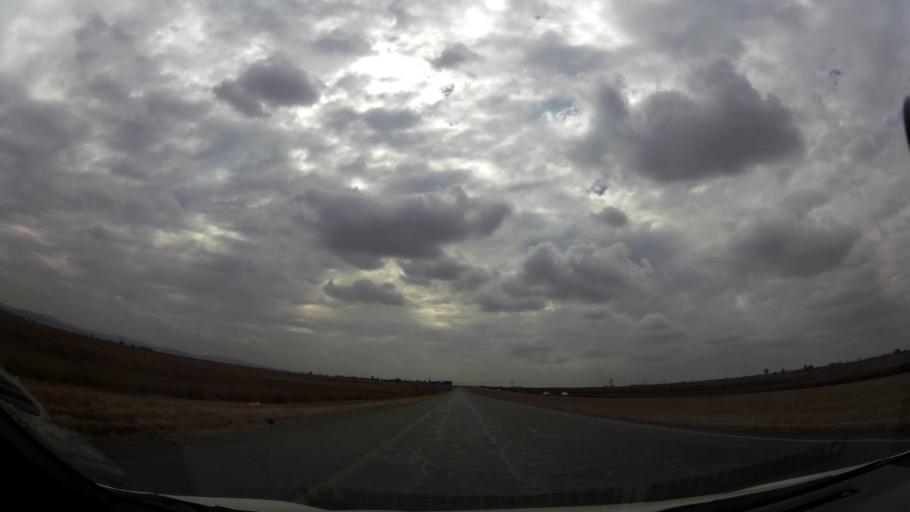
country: ZA
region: Gauteng
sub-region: Ekurhuleni Metropolitan Municipality
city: Germiston
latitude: -26.3709
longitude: 28.0918
